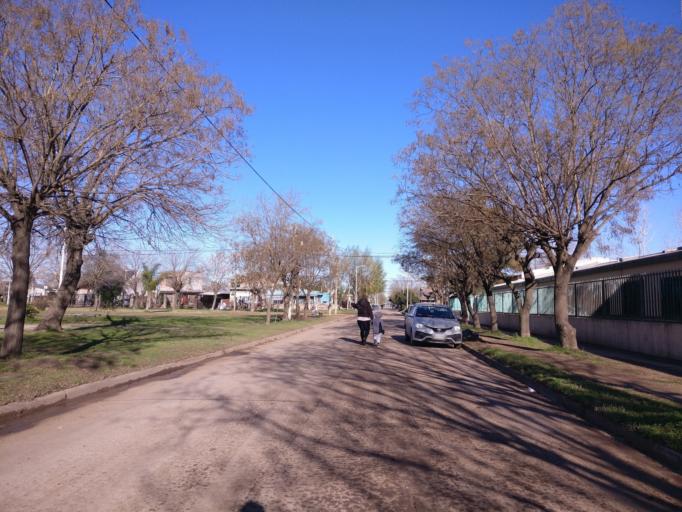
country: AR
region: Buenos Aires
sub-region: Partido de Ezeiza
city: Ezeiza
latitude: -34.9390
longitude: -58.6089
